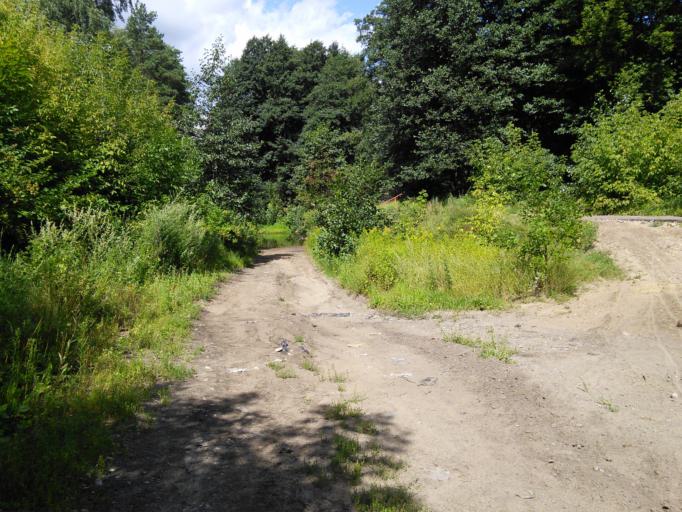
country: RU
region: Moskovskaya
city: Kratovo
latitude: 55.5939
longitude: 38.1560
